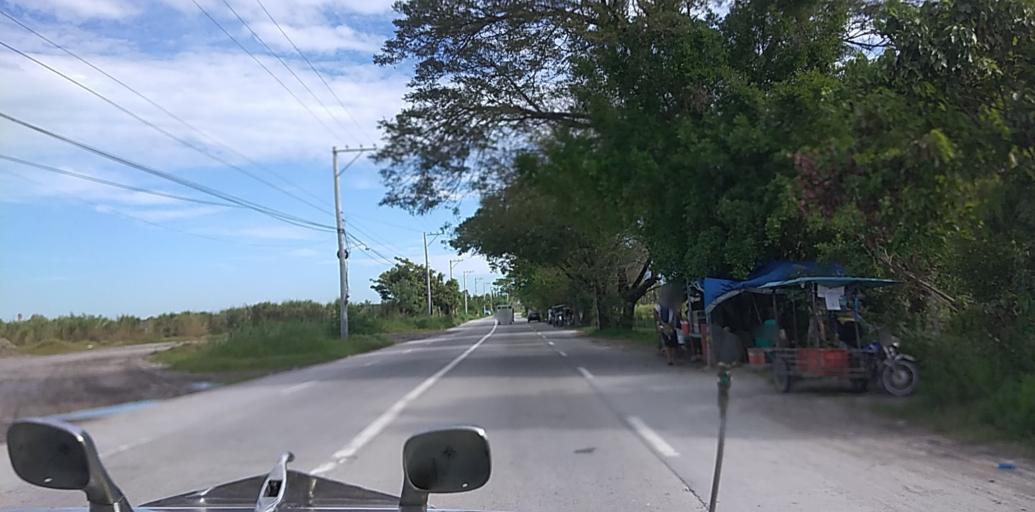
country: PH
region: Central Luzon
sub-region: Province of Pampanga
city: Malino
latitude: 15.1211
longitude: 120.6665
